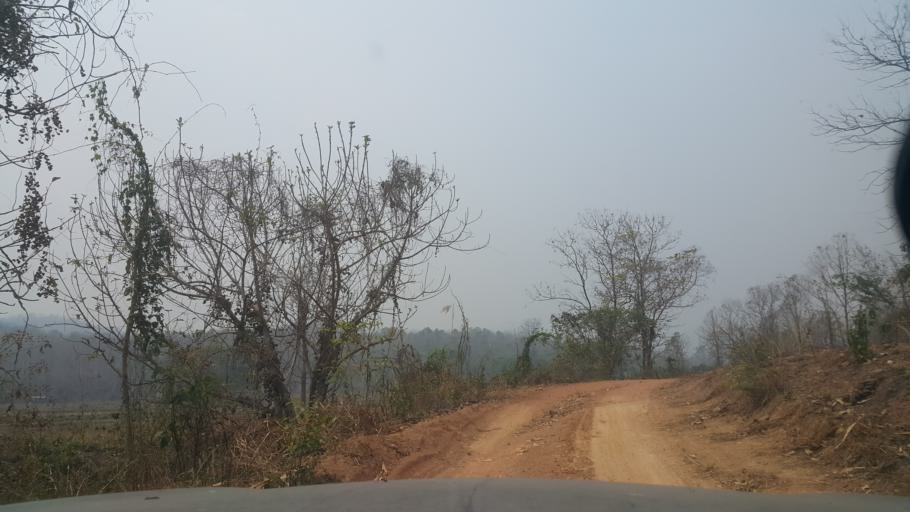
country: TH
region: Lampang
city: Hang Chat
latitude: 18.3126
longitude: 99.2508
